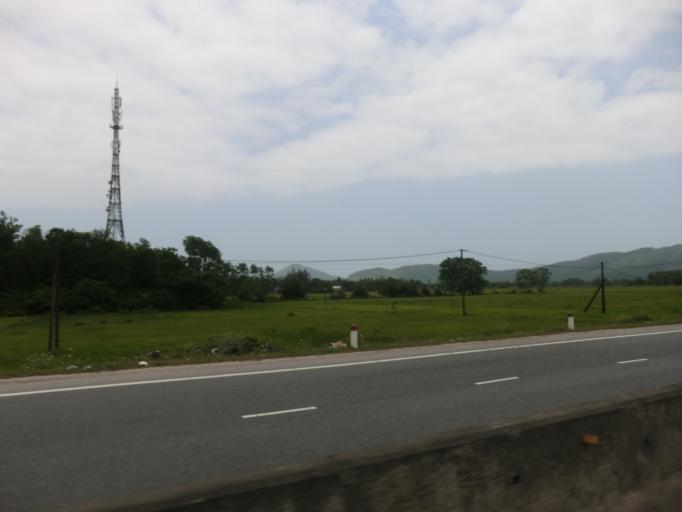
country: VN
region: Thua Thien-Hue
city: Phu Loc
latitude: 16.2707
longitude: 108.0096
